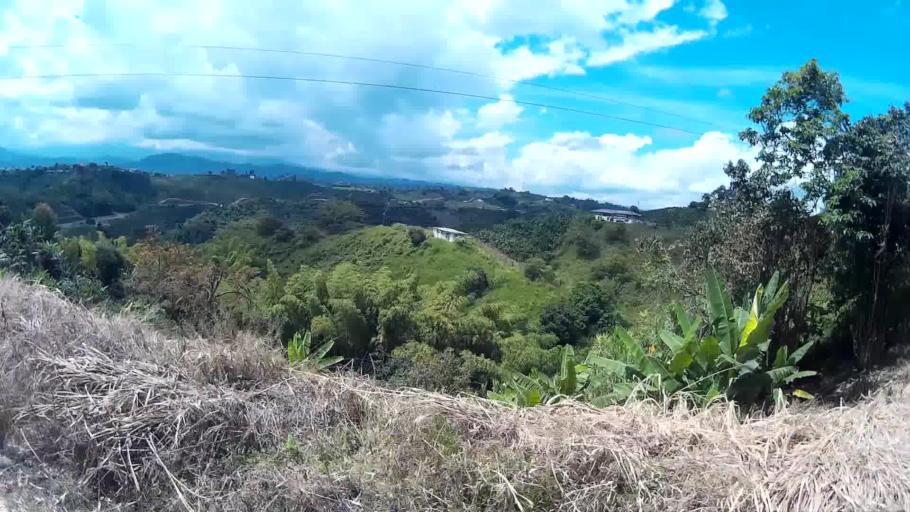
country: CO
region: Risaralda
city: Pereira
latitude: 4.7733
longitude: -75.7185
